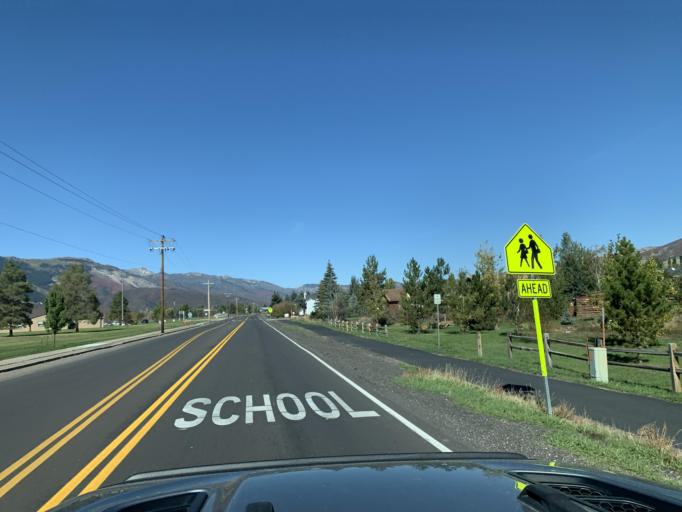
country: US
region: Utah
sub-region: Weber County
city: Wolf Creek
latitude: 41.3074
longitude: -111.8301
